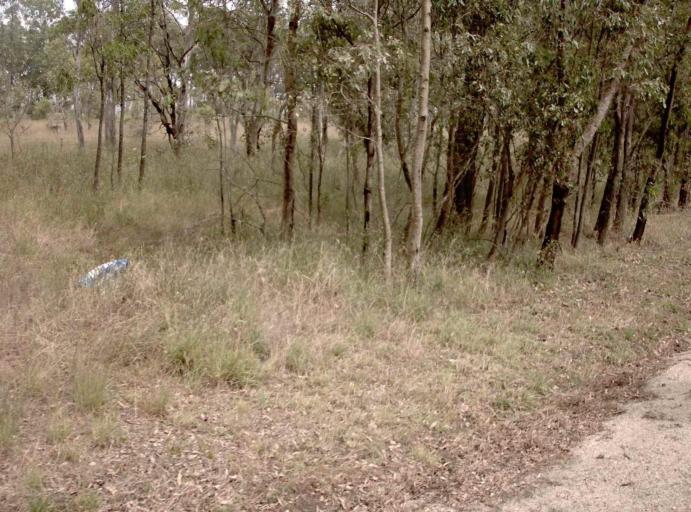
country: AU
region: Victoria
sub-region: Wellington
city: Sale
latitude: -37.9093
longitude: 147.0796
